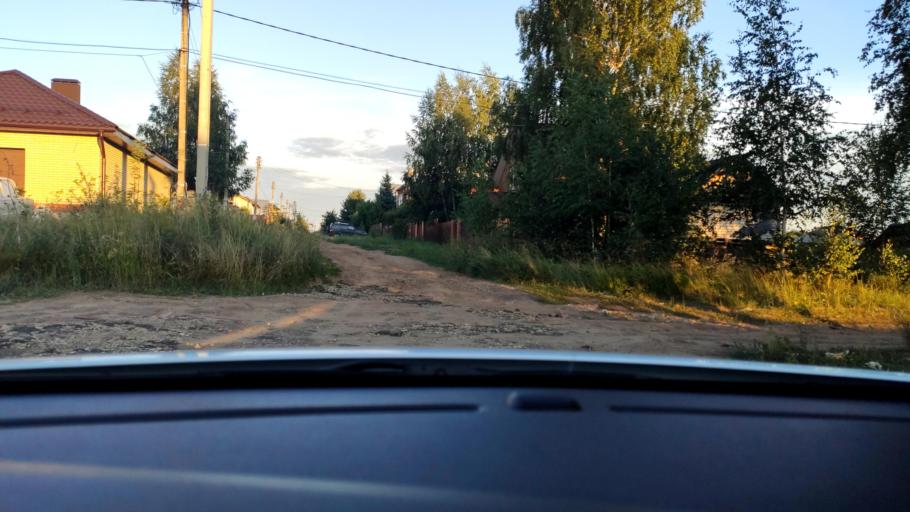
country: RU
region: Tatarstan
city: Stolbishchi
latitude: 55.7582
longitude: 49.2807
